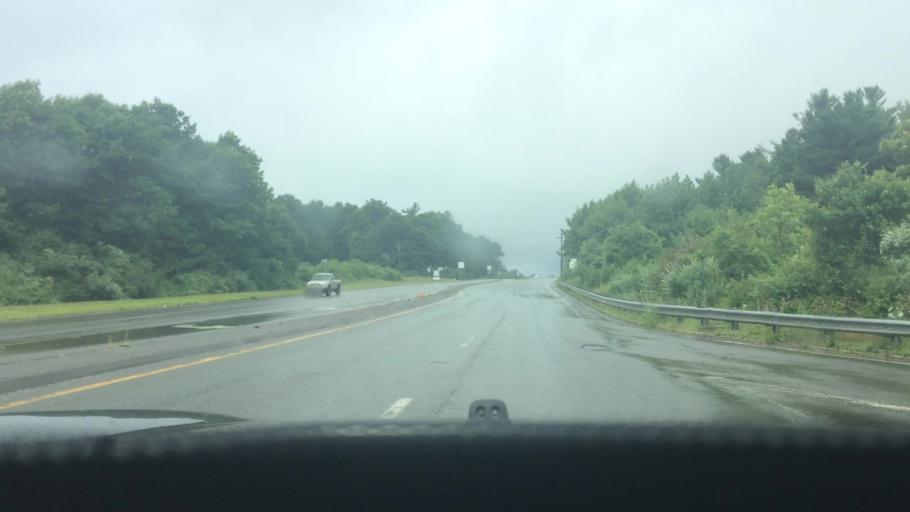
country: US
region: Massachusetts
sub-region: Worcester County
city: Westminster
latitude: 42.5616
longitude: -71.9363
